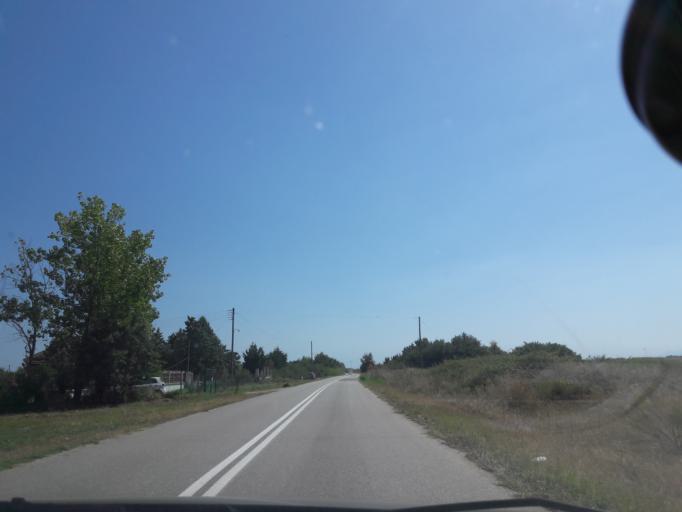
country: GR
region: Central Macedonia
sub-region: Nomos Chalkidikis
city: Nea Kallikrateia
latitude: 40.3306
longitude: 23.0240
